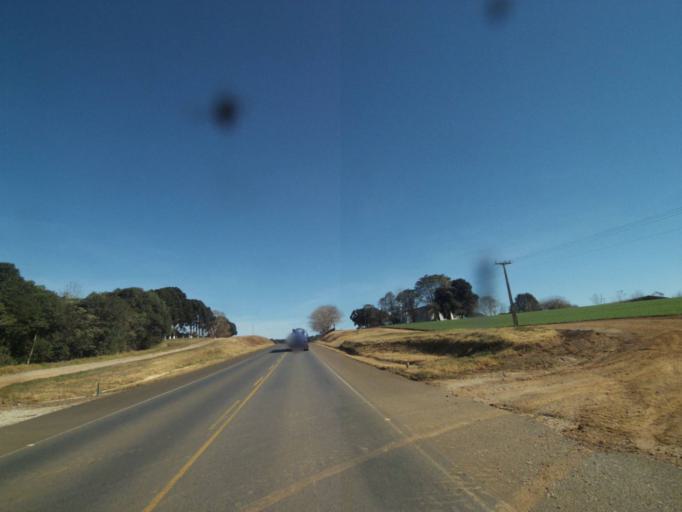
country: BR
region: Parana
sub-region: Tibagi
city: Tibagi
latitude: -24.4694
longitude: -50.4426
